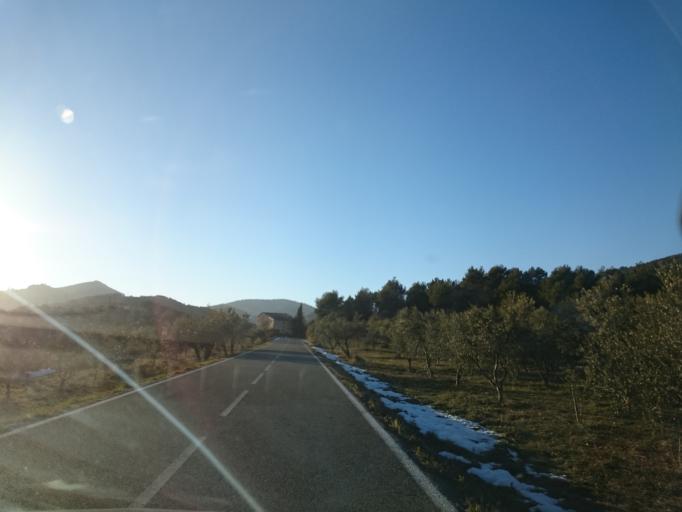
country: ES
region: Catalonia
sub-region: Provincia de Tarragona
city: la Bisbal del Penedes
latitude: 41.3742
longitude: 1.4919
